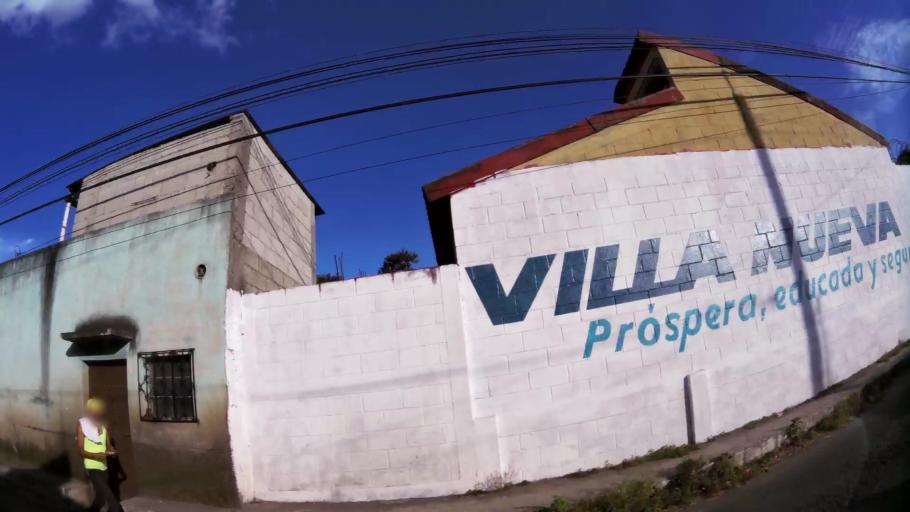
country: GT
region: Guatemala
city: Villa Nueva
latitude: 14.5216
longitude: -90.5786
